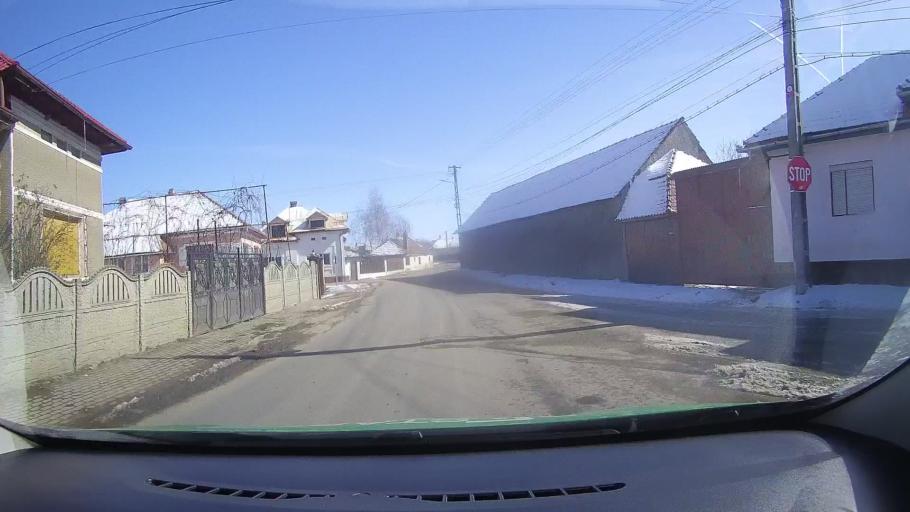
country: RO
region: Brasov
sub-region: Comuna Dragus
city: Dragus
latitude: 45.7613
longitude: 24.7787
